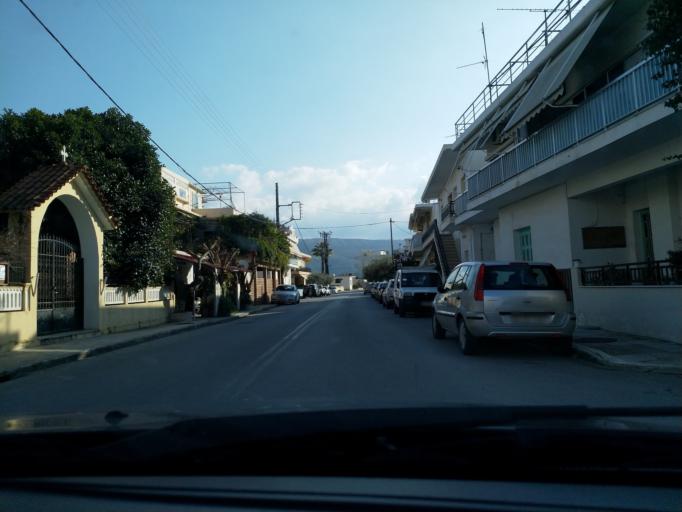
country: GR
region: Crete
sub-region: Nomos Chanias
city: Chania
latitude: 35.5022
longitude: 24.0255
